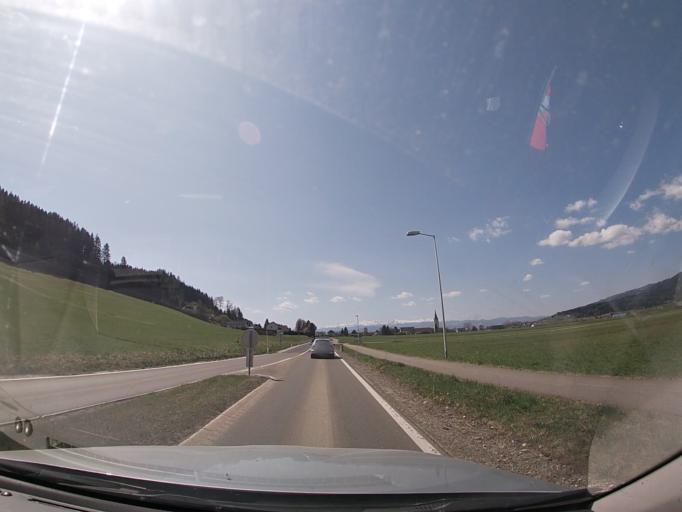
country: AT
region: Styria
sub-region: Politischer Bezirk Murtal
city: Sankt Margarethen bei Knittelfeld
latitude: 47.2315
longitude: 14.8643
